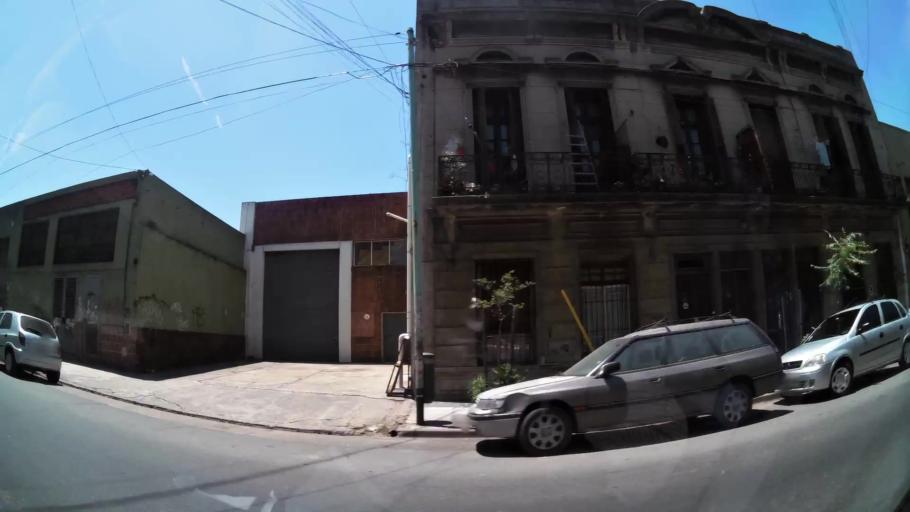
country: AR
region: Buenos Aires
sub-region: Partido de Avellaneda
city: Avellaneda
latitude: -34.6392
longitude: -58.3811
